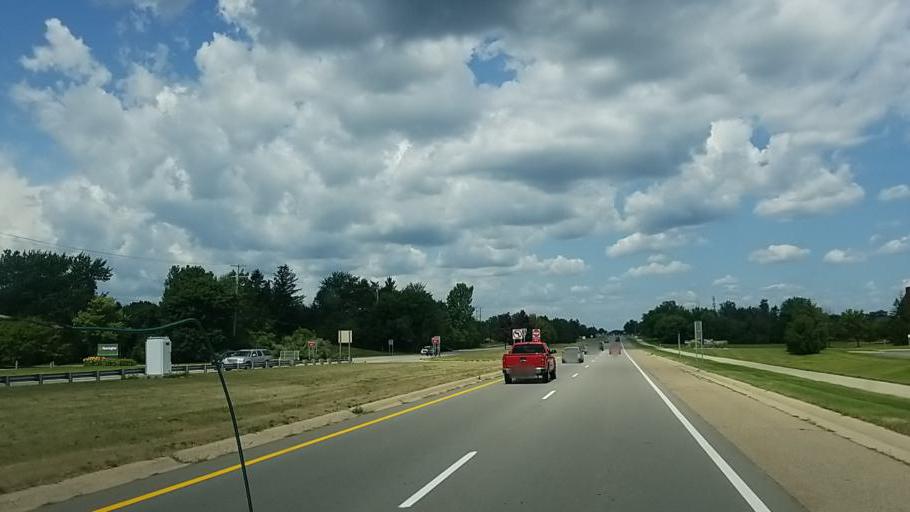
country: US
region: Michigan
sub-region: Kent County
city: East Grand Rapids
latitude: 42.9865
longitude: -85.5903
